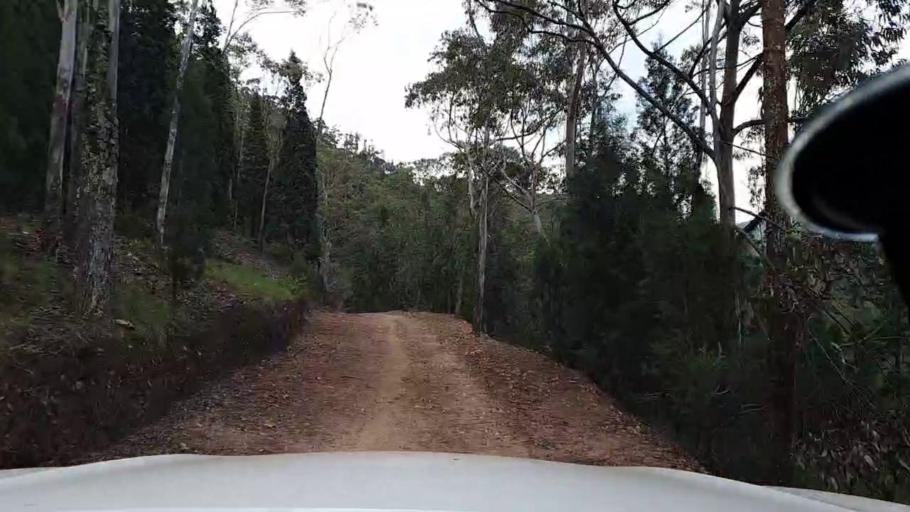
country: RW
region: Southern Province
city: Gitarama
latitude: -1.8084
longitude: 29.8035
